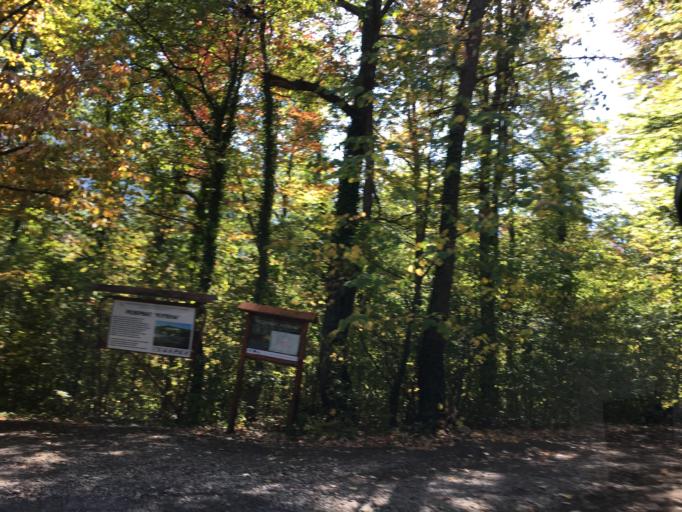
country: BG
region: Pazardzhik
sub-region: Obshtina Peshtera
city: Peshtera
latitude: 42.0001
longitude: 24.2818
